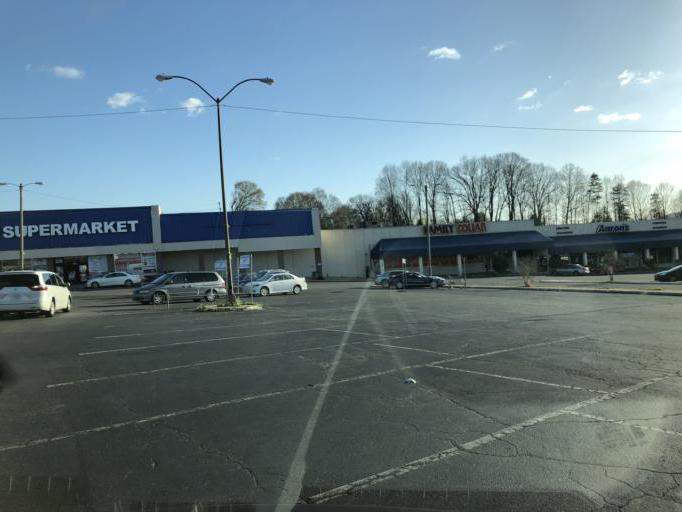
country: US
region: North Carolina
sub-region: Gaston County
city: Gastonia
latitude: 35.2579
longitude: -81.2276
